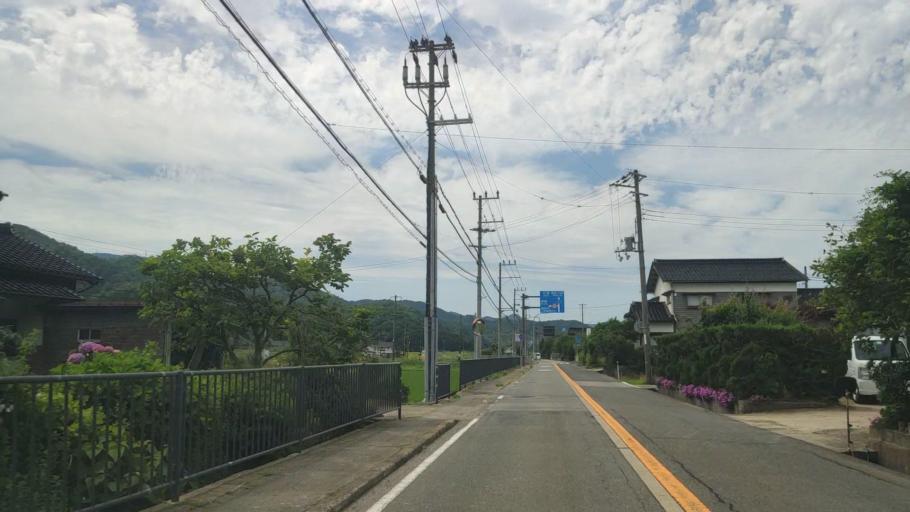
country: JP
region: Hyogo
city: Toyooka
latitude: 35.6443
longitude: 134.7581
